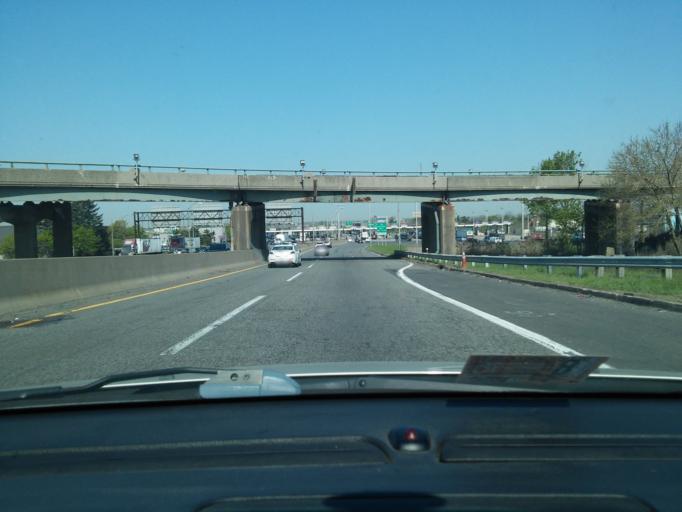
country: US
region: New Jersey
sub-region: Essex County
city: Newark
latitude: 40.7071
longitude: -74.1531
